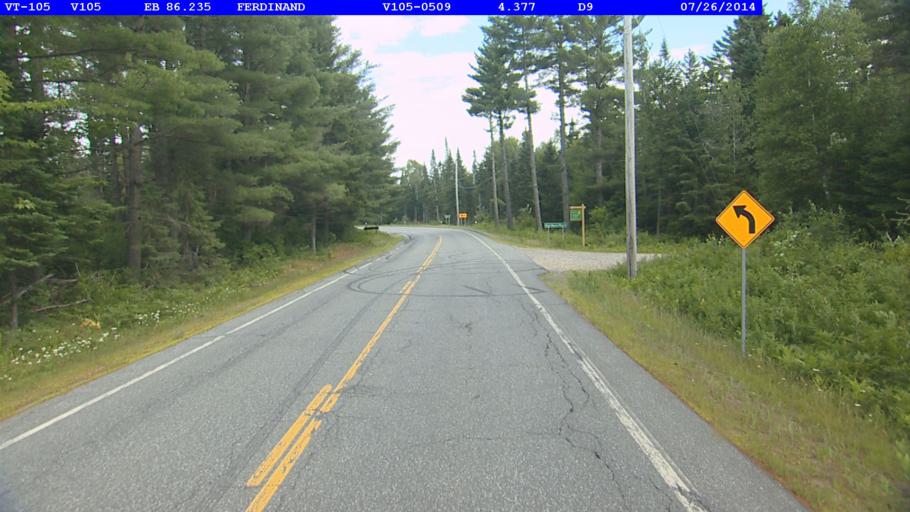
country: US
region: New Hampshire
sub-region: Coos County
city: Stratford
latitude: 44.7606
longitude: -71.7280
